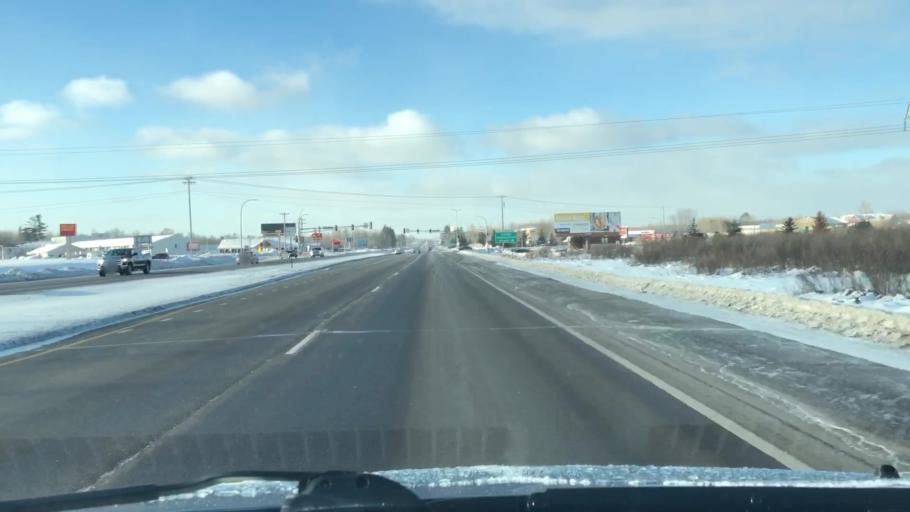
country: US
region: Minnesota
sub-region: Saint Louis County
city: Hermantown
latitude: 46.8136
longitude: -92.1726
